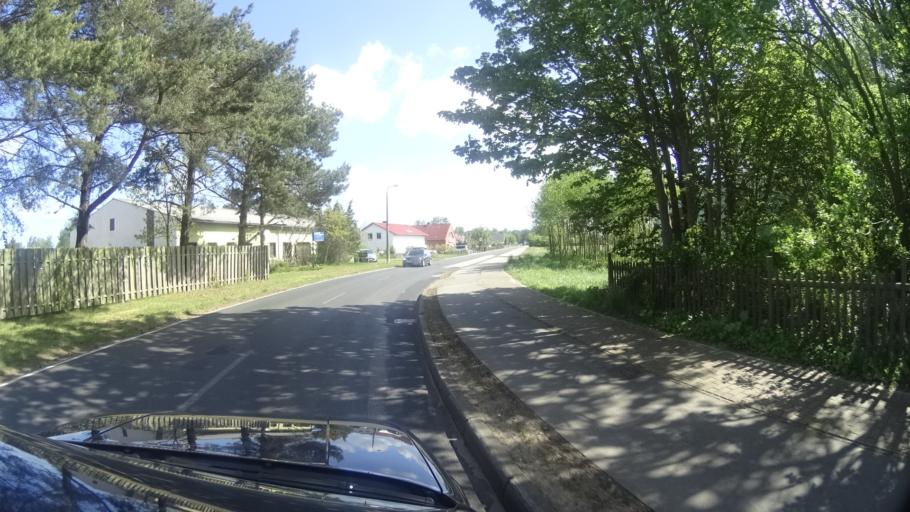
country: DE
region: Mecklenburg-Vorpommern
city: Born
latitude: 54.3680
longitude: 12.6087
